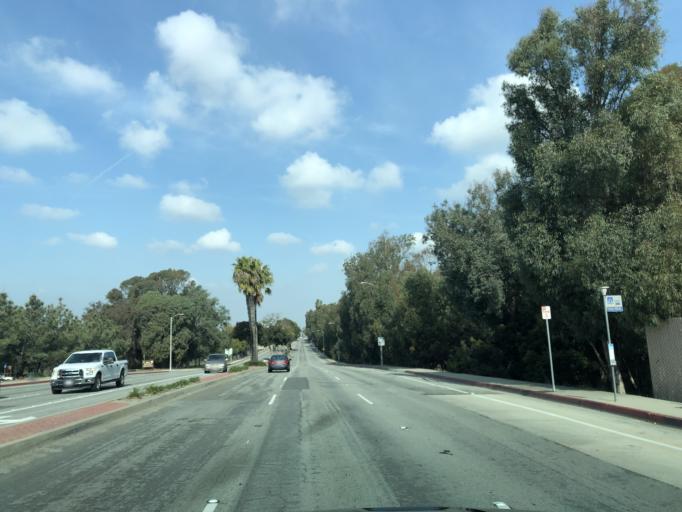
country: US
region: California
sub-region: Orange County
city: Huntington Beach
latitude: 33.7014
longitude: -118.0063
